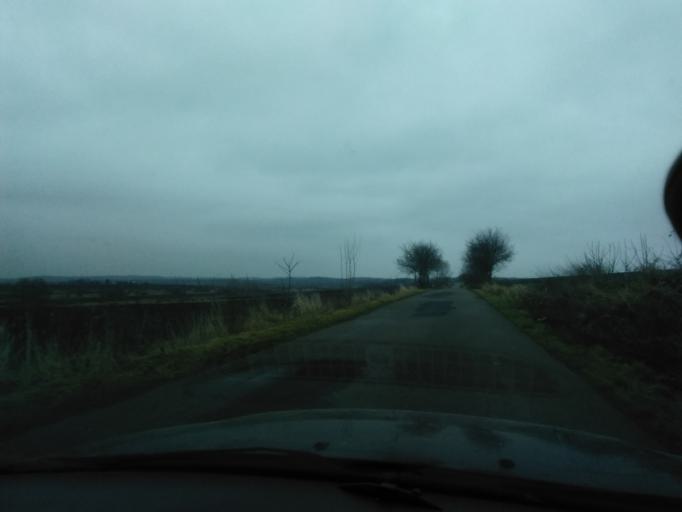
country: PL
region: Subcarpathian Voivodeship
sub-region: Powiat jaroslawski
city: Pruchnik
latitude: 49.9356
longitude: 22.5430
